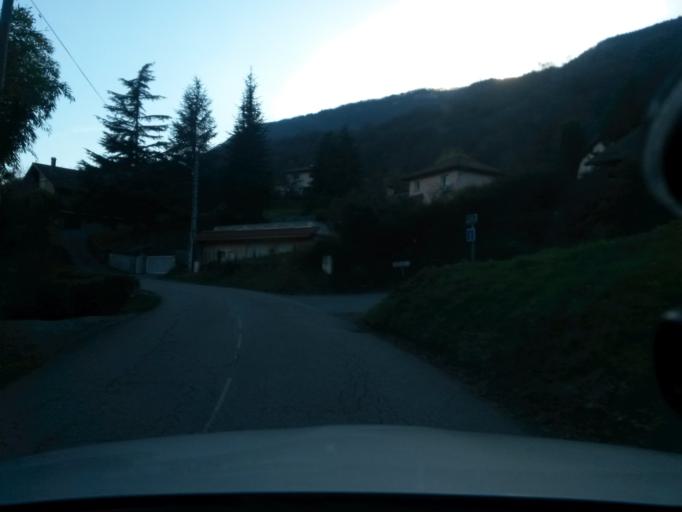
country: FR
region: Rhone-Alpes
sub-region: Departement de l'Isere
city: Le Touvet
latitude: 45.3556
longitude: 5.9443
